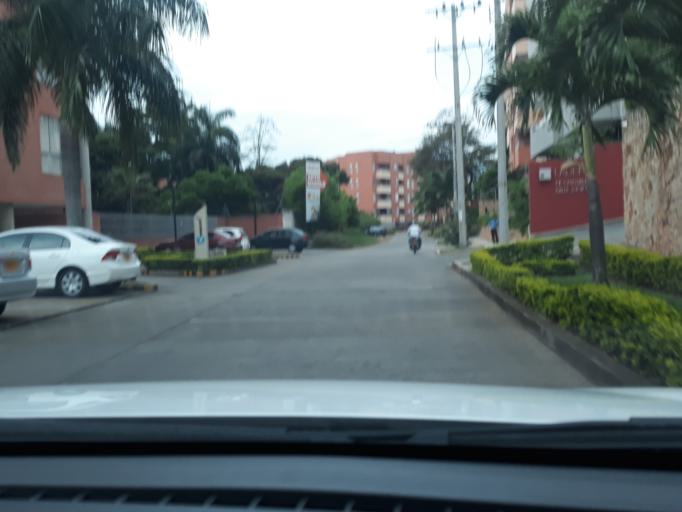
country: CO
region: Valle del Cauca
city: Cali
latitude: 3.4299
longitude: -76.5488
